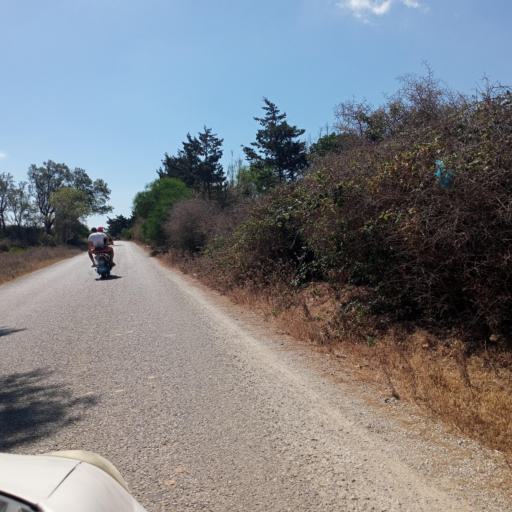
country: TN
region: Nabul
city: Qulaybiyah
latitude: 36.8611
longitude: 11.0422
